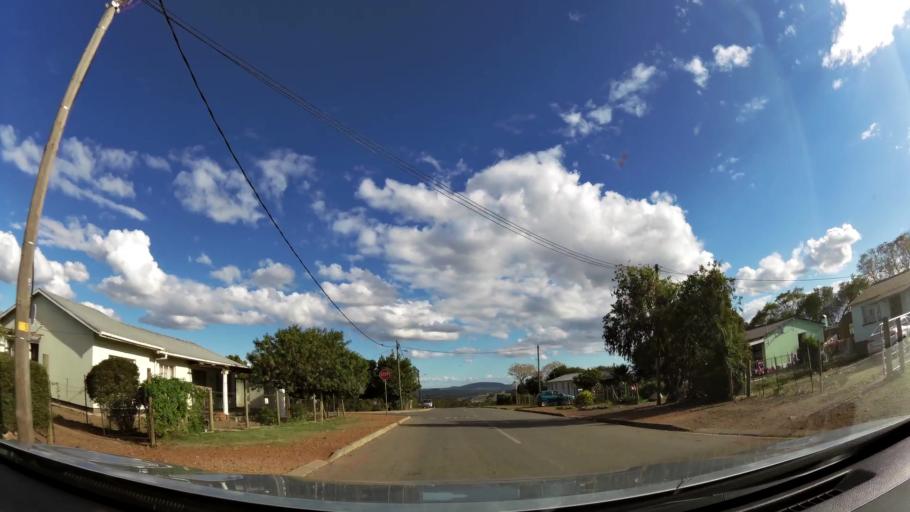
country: ZA
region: Western Cape
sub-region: Overberg District Municipality
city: Swellendam
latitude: -34.0336
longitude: 20.4394
